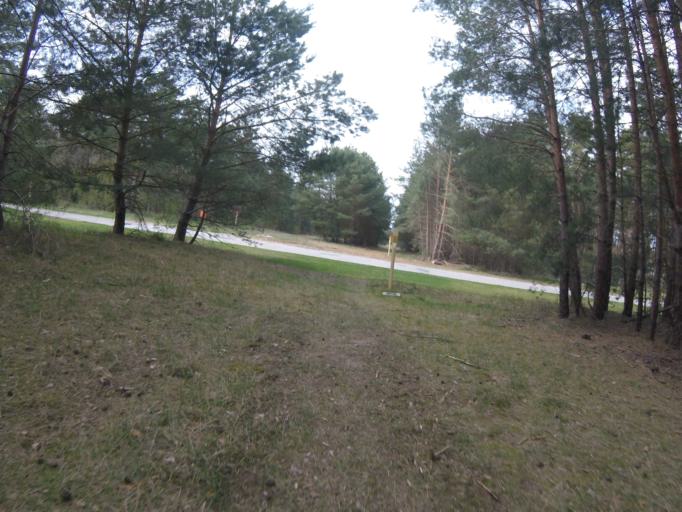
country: DE
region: Brandenburg
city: Bestensee
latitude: 52.2152
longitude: 13.6084
